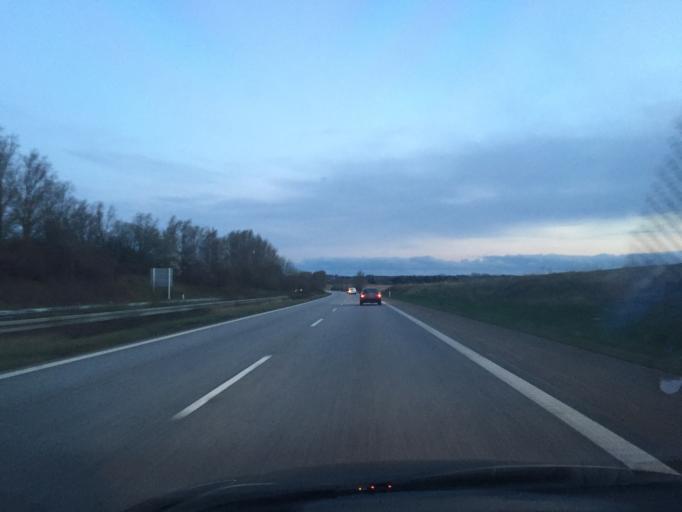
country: DK
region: Capital Region
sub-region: Fredensborg Kommune
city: Niva
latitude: 55.9520
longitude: 12.4788
